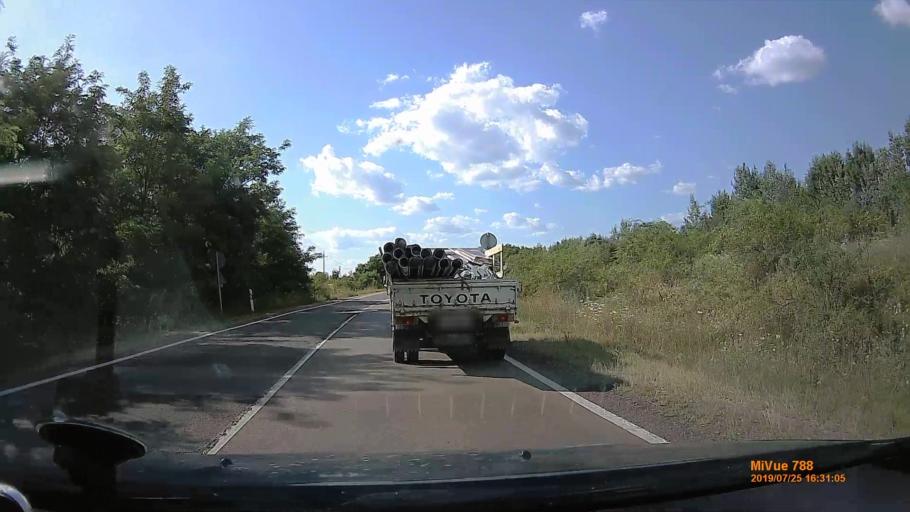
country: HU
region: Heves
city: Karacsond
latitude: 47.7325
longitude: 20.0452
